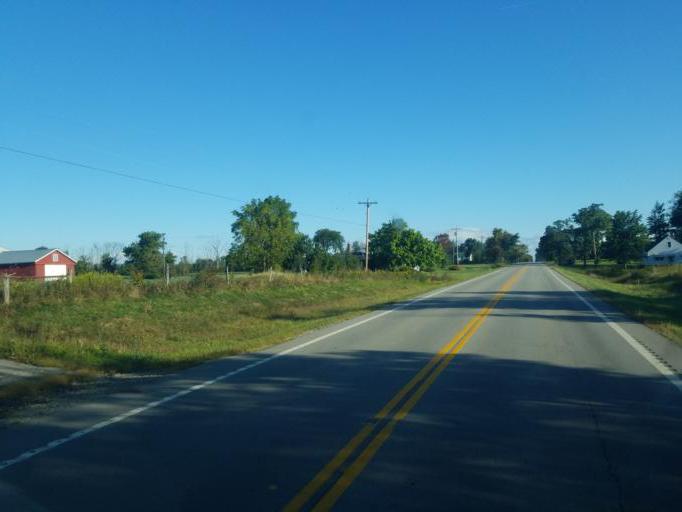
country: US
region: Ohio
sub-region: Lorain County
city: Camden
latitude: 41.1576
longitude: -82.3100
